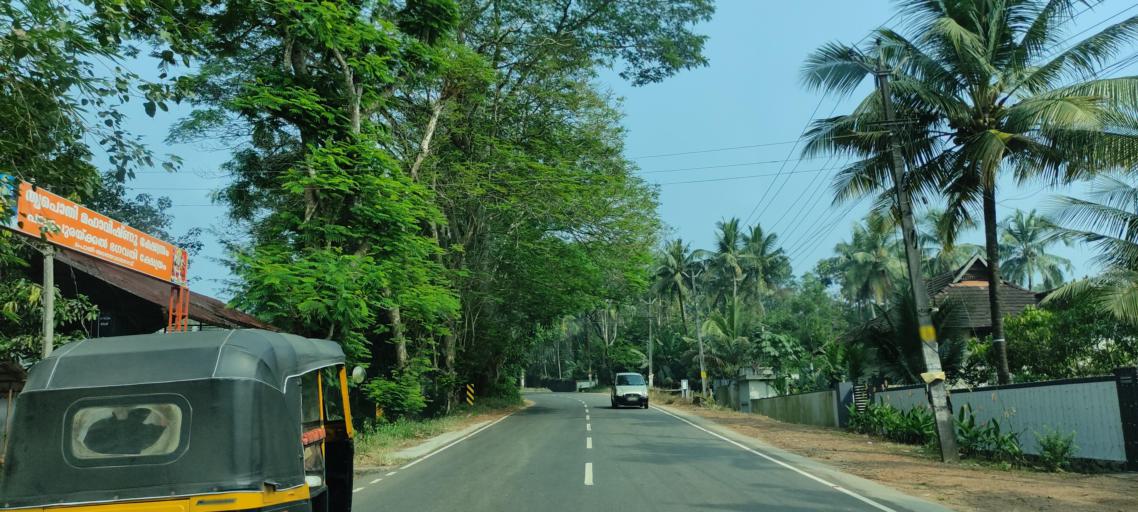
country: IN
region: Kerala
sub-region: Ernakulam
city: Piravam
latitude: 9.7948
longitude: 76.4682
